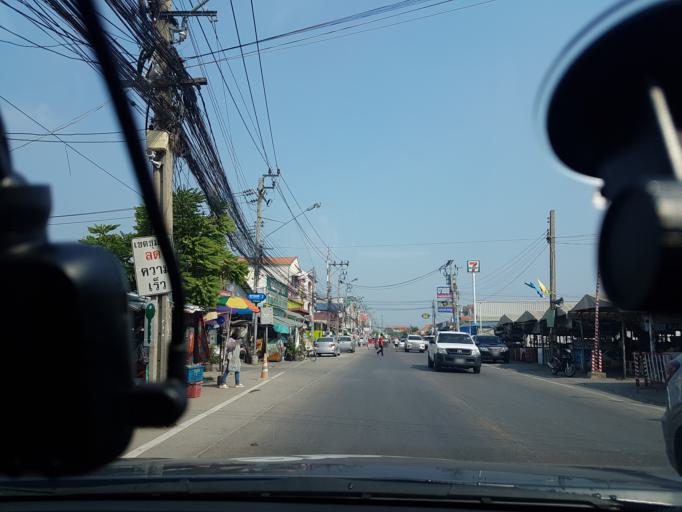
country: TH
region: Bangkok
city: Khan Na Yao
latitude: 13.8417
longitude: 100.7042
